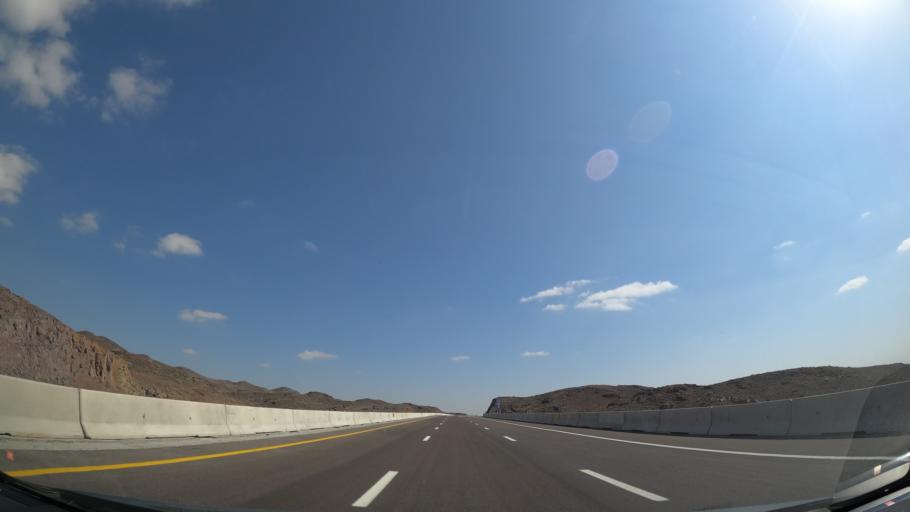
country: IR
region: Alborz
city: Eshtehard
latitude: 35.6614
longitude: 50.6557
